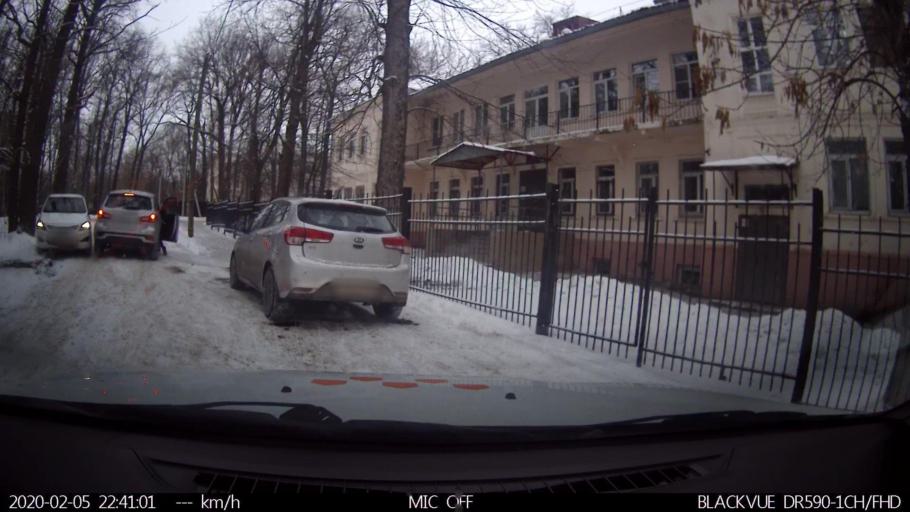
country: RU
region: Nizjnij Novgorod
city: Imeni Stepana Razina
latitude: 54.7217
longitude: 44.3318
